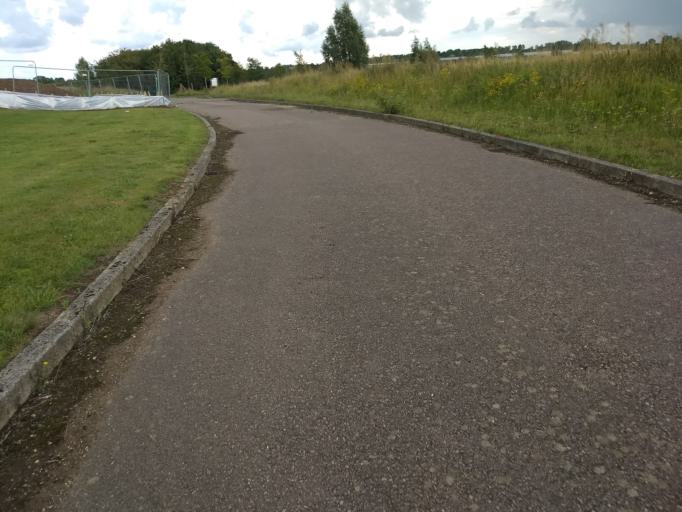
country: GB
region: England
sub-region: Milton Keynes
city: Shenley Church End
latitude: 51.9912
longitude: -0.8027
